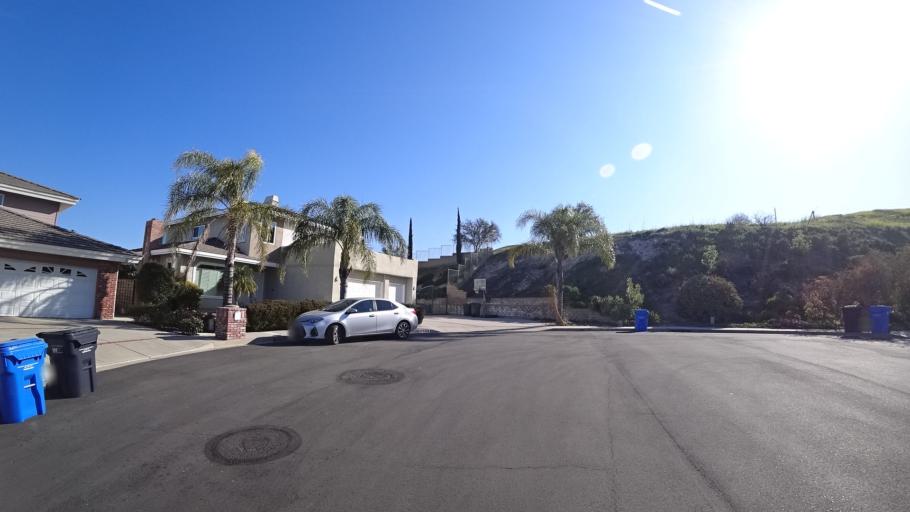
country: US
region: California
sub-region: Ventura County
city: Thousand Oaks
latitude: 34.1865
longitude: -118.8362
